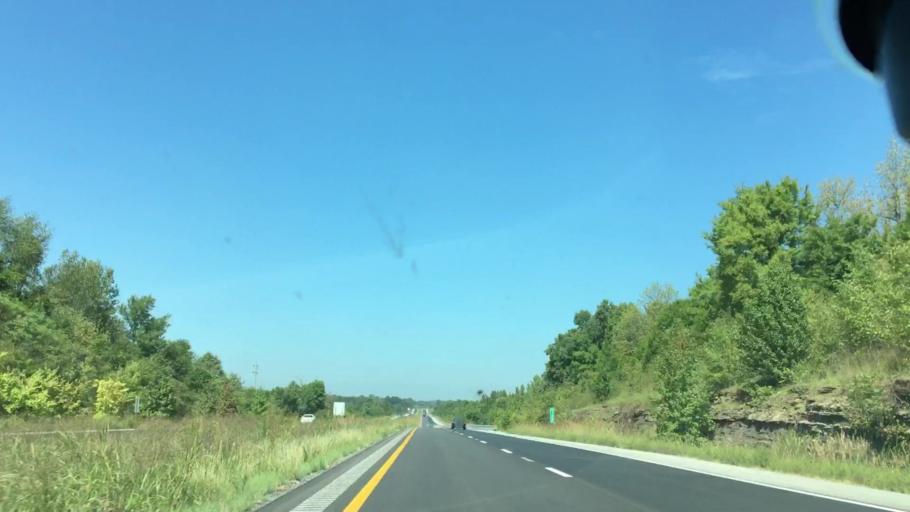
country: US
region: Kentucky
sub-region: Hopkins County
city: Madisonville
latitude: 37.4336
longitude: -87.4725
